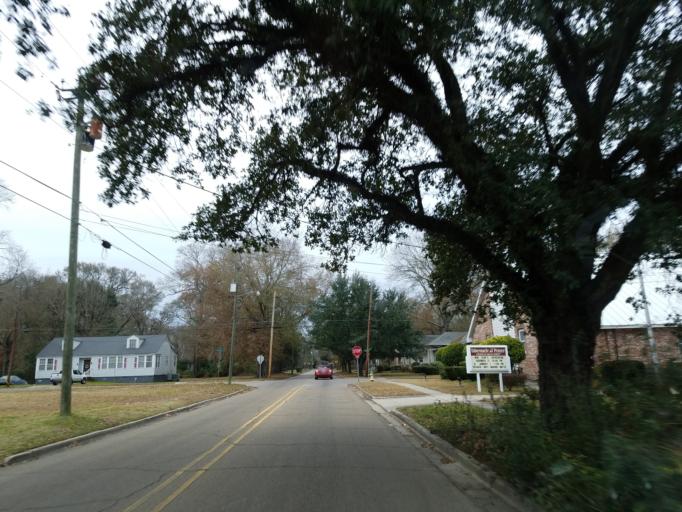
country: US
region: Mississippi
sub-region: Forrest County
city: Hattiesburg
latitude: 31.3199
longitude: -89.2843
